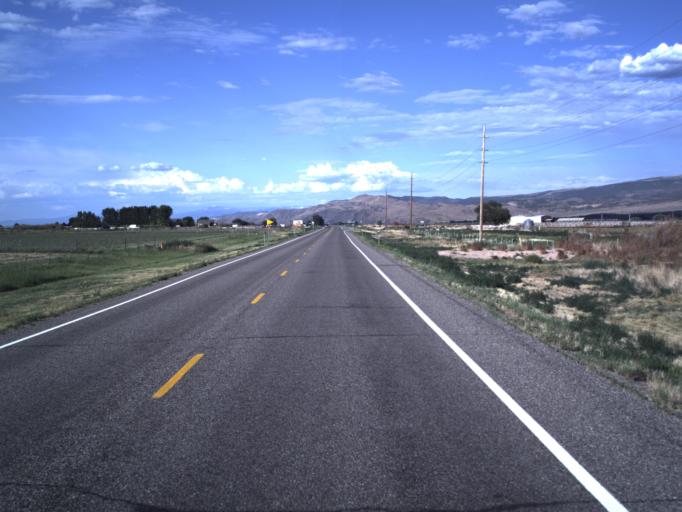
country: US
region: Utah
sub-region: Sevier County
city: Monroe
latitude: 38.6852
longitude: -112.1282
